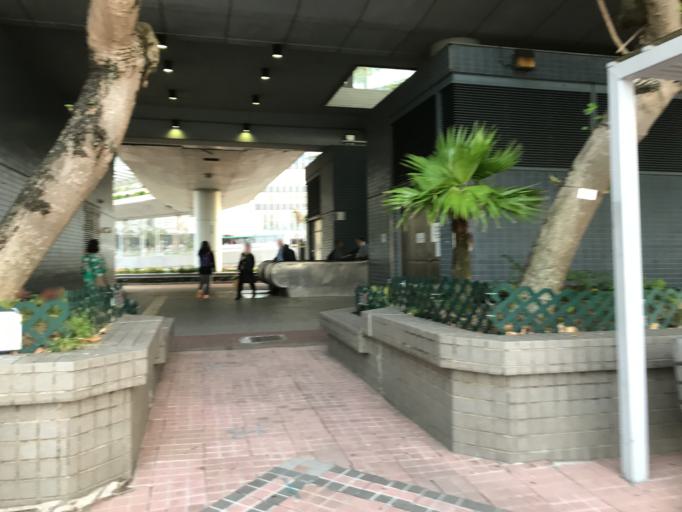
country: HK
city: Hong Kong
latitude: 22.2876
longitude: 114.1579
